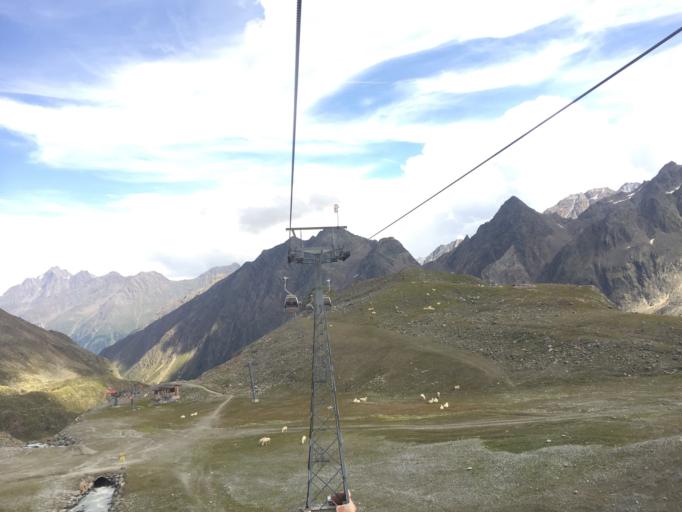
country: AT
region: Tyrol
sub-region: Politischer Bezirk Imst
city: Soelden
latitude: 46.9968
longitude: 11.1220
